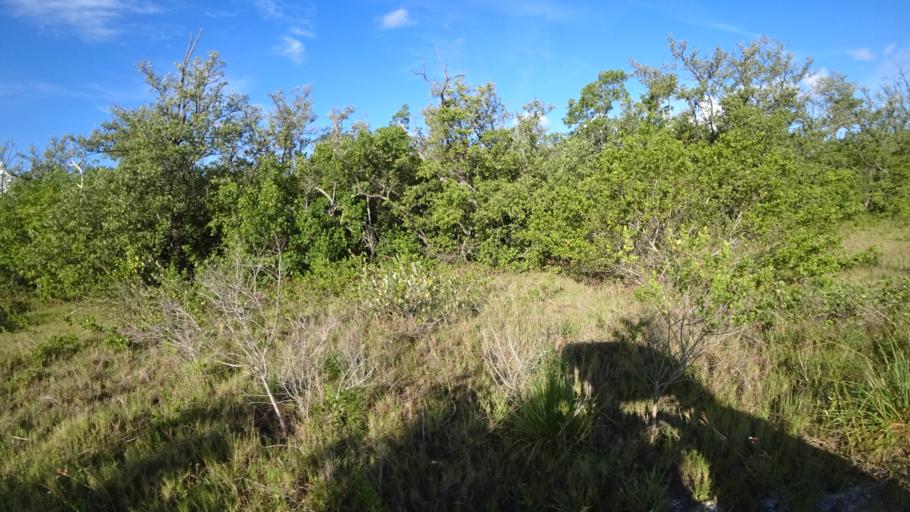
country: US
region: Florida
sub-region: Manatee County
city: Holmes Beach
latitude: 27.5123
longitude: -82.6729
